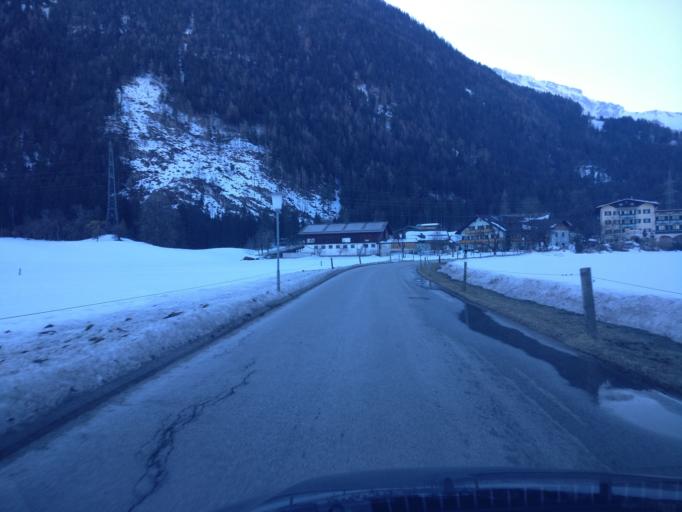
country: AT
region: Salzburg
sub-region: Politischer Bezirk Hallein
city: Golling an der Salzach
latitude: 47.6018
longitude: 13.1468
